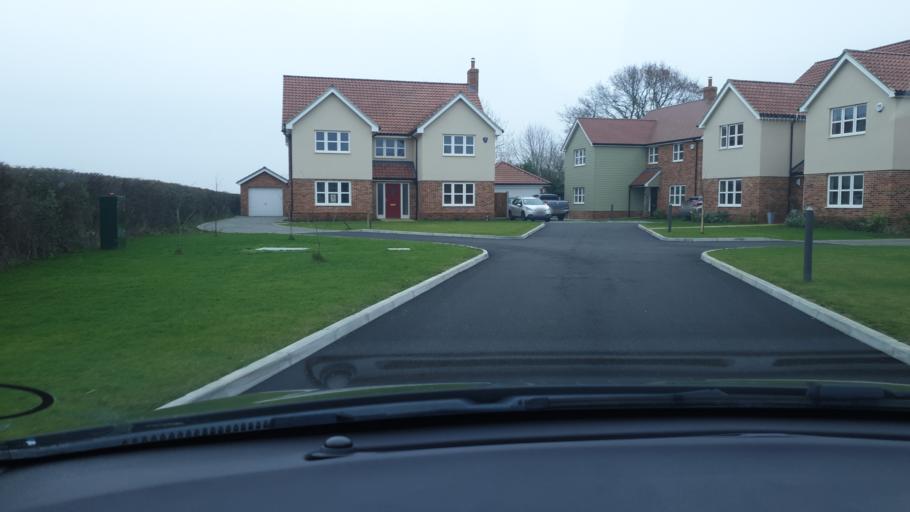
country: GB
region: England
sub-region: Essex
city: Great Bentley
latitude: 51.8428
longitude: 1.0751
